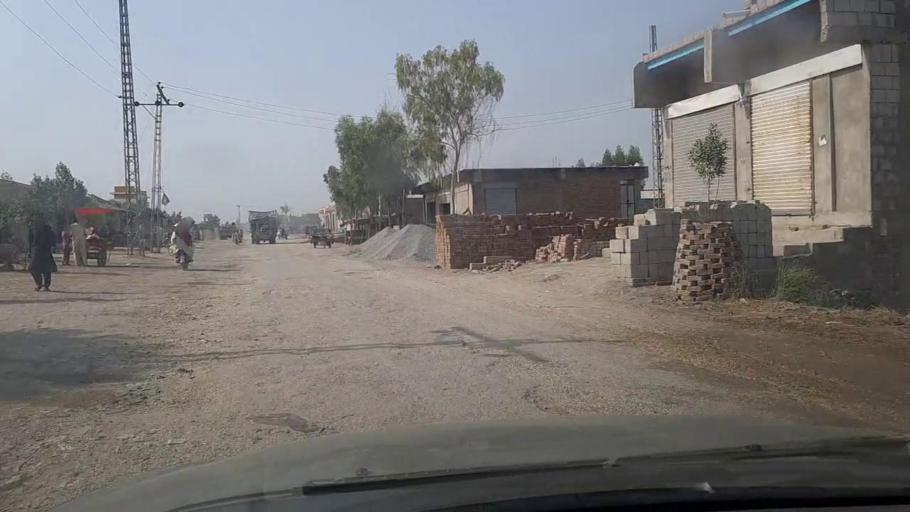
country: PK
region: Sindh
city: Mirpur Mathelo
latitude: 28.0125
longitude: 69.5474
